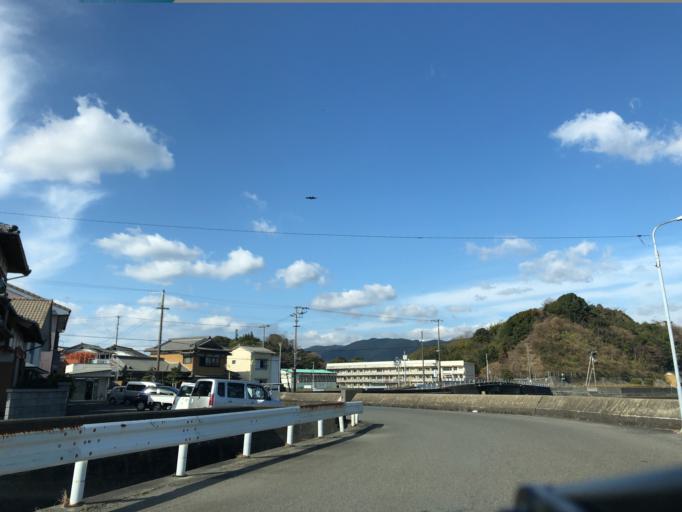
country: JP
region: Kochi
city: Sukumo
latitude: 32.9175
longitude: 132.7036
